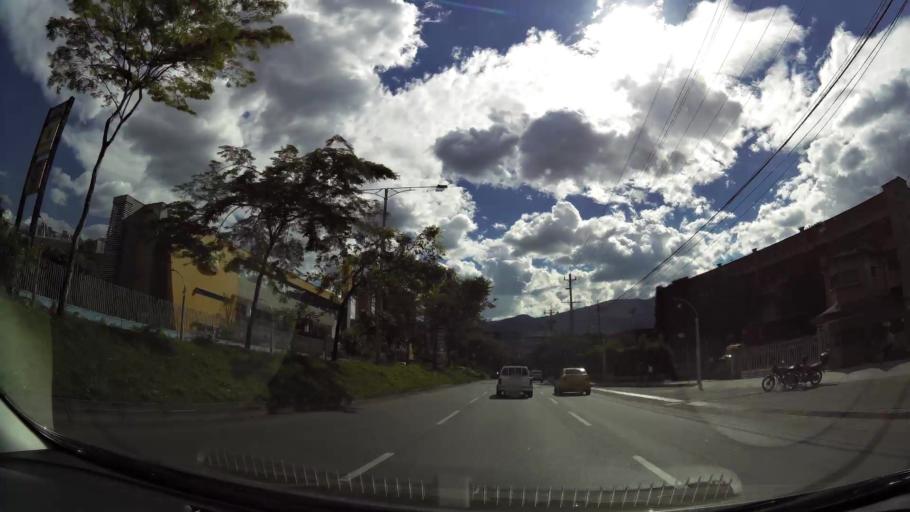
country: CO
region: Antioquia
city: Sabaneta
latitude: 6.1598
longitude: -75.6068
